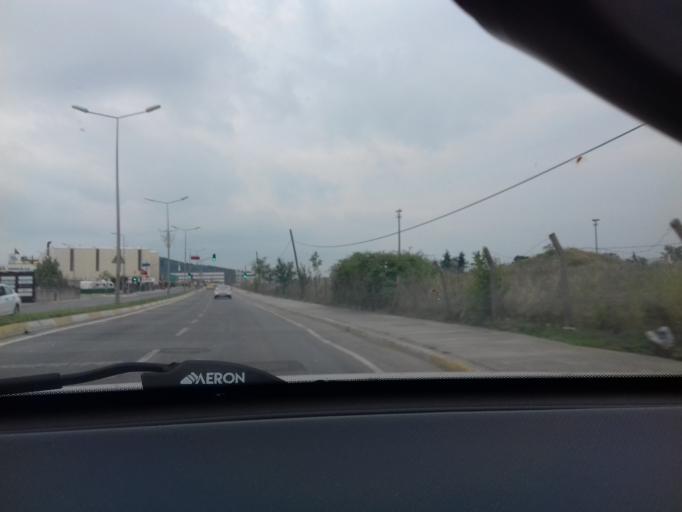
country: TR
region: Istanbul
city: Icmeler
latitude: 40.8902
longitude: 29.3537
